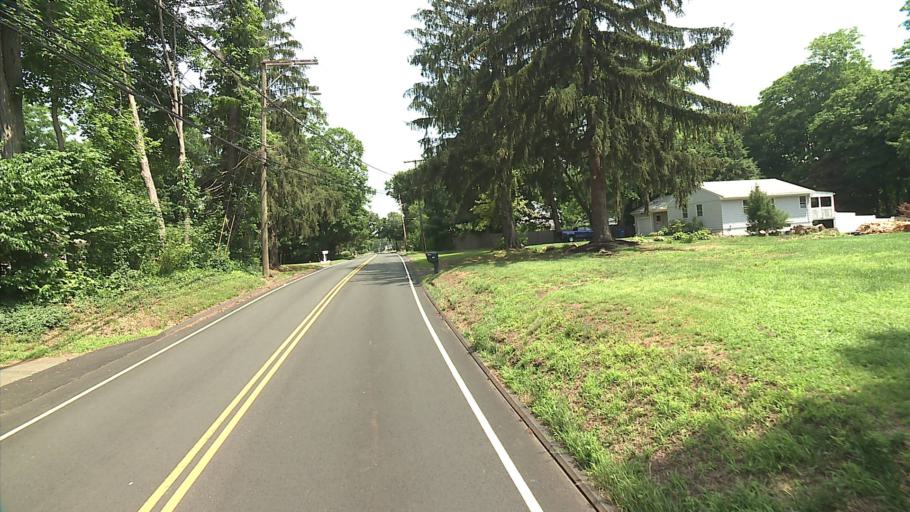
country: US
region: Connecticut
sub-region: New Haven County
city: Branford
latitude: 41.3253
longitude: -72.8139
